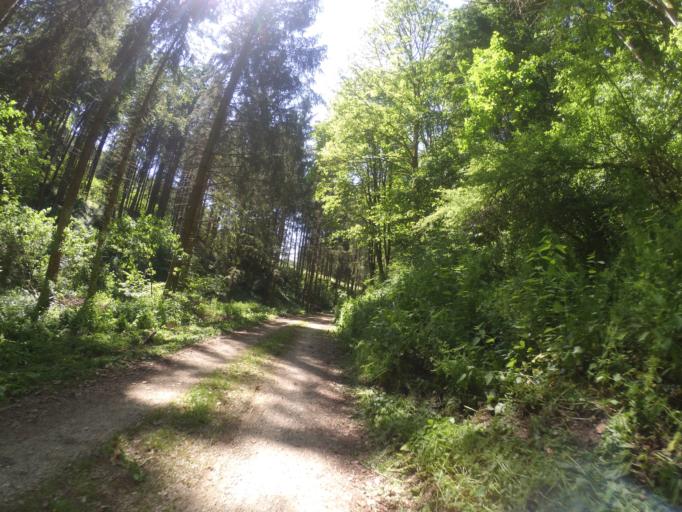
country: DE
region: Baden-Wuerttemberg
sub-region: Tuebingen Region
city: Berghulen
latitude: 48.4855
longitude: 9.7925
